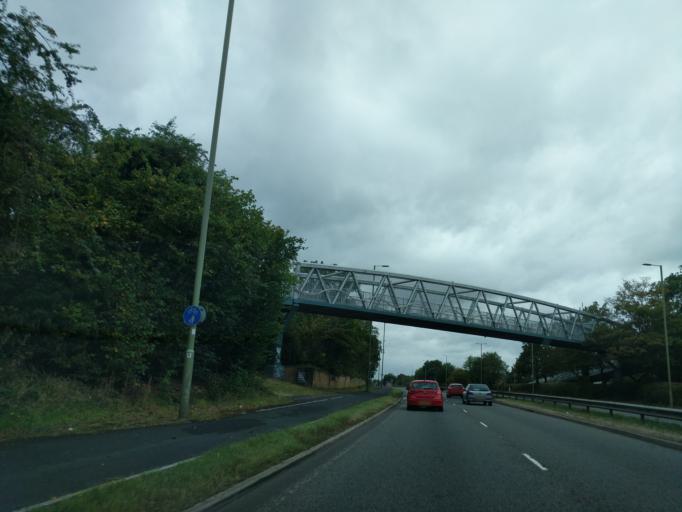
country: GB
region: England
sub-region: Oxfordshire
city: Oxford
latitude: 51.7878
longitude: -1.2602
